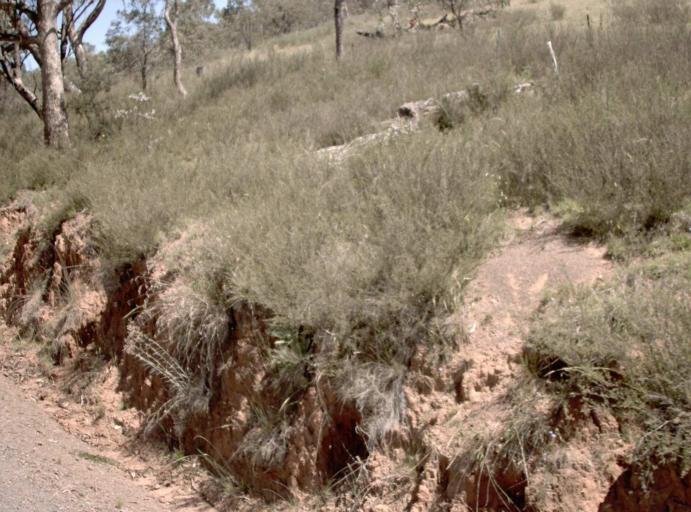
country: AU
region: New South Wales
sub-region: Snowy River
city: Jindabyne
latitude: -37.0487
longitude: 148.5628
